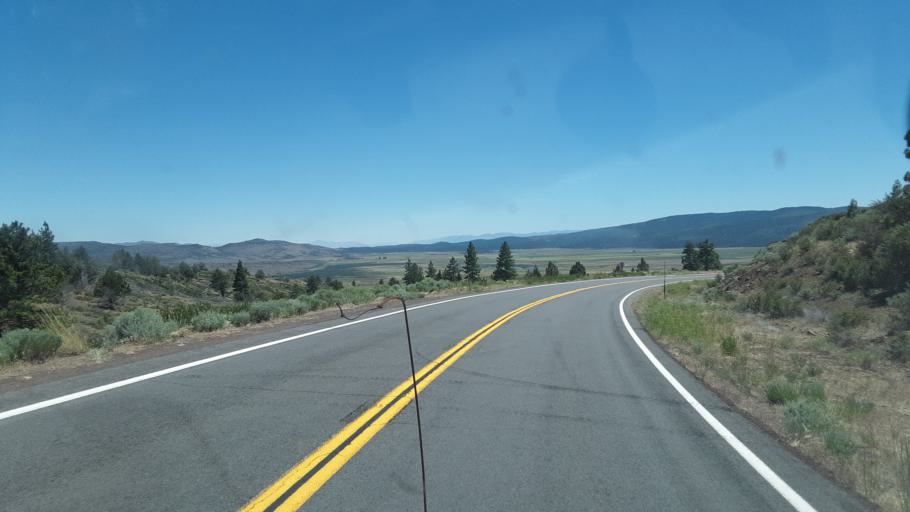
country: US
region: California
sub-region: Lassen County
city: Susanville
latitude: 40.6065
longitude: -120.6419
